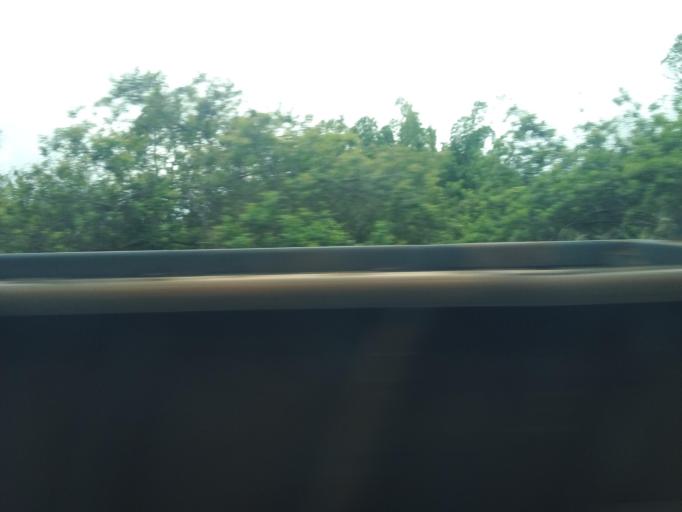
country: BR
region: Minas Gerais
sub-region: Rio Piracicaba
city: Rio Piracicaba
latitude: -19.9682
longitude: -43.2522
